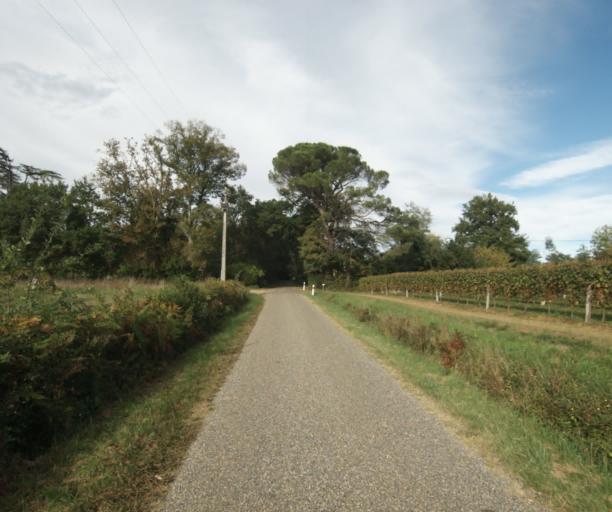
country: FR
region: Midi-Pyrenees
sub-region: Departement du Gers
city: Le Houga
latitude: 43.8794
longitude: -0.1677
